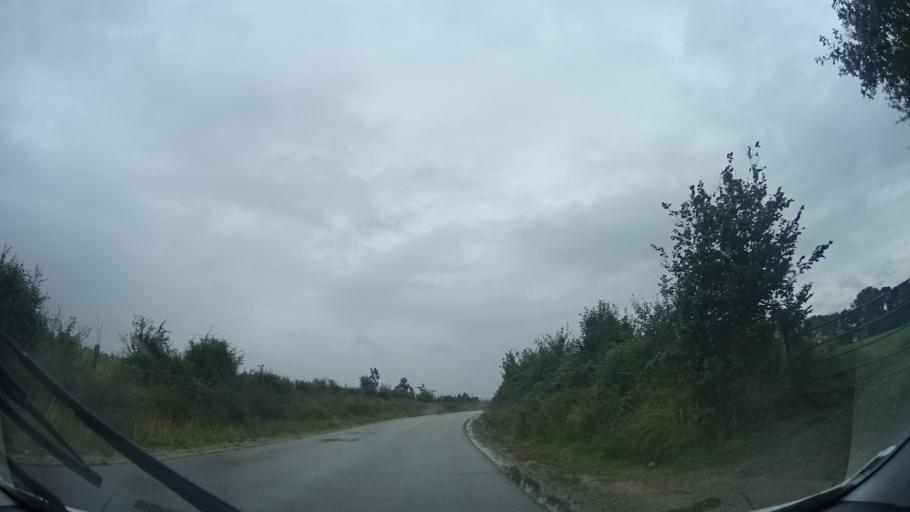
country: FR
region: Lower Normandy
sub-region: Departement de la Manche
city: Urville-Nacqueville
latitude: 49.5955
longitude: -1.7651
